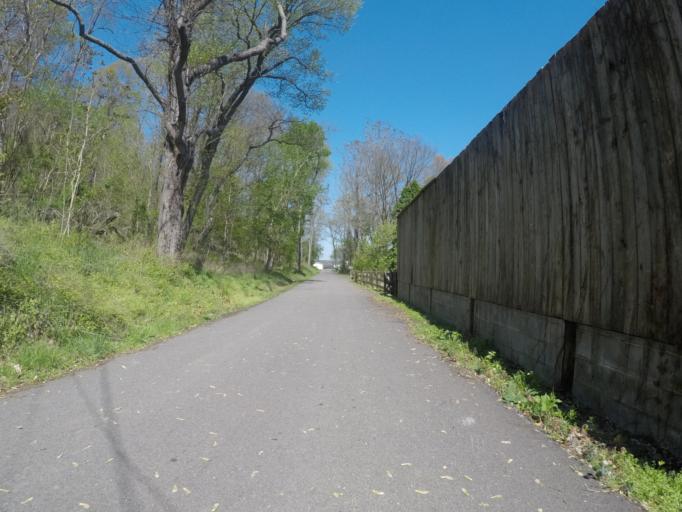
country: US
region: West Virginia
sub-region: Wayne County
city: Kenova
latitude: 38.3893
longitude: -82.5860
